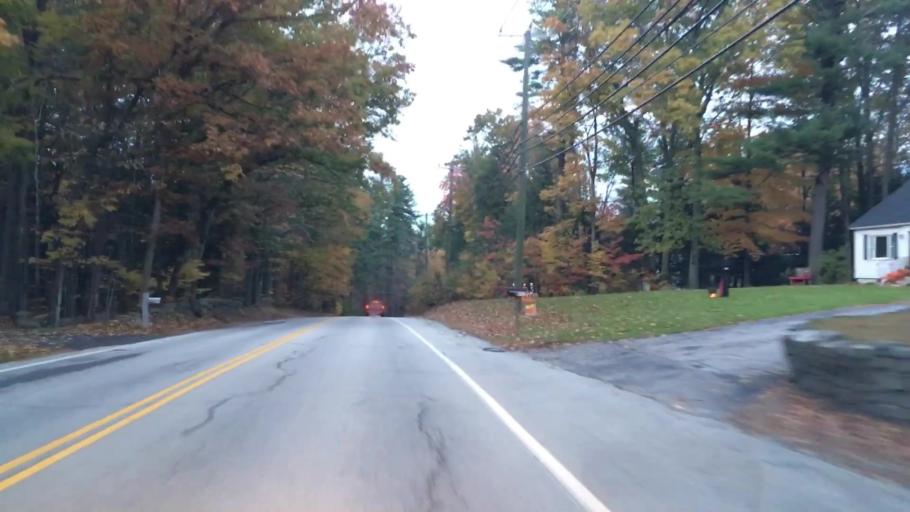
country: US
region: New Hampshire
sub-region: Hillsborough County
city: Milford
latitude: 42.8568
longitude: -71.6348
